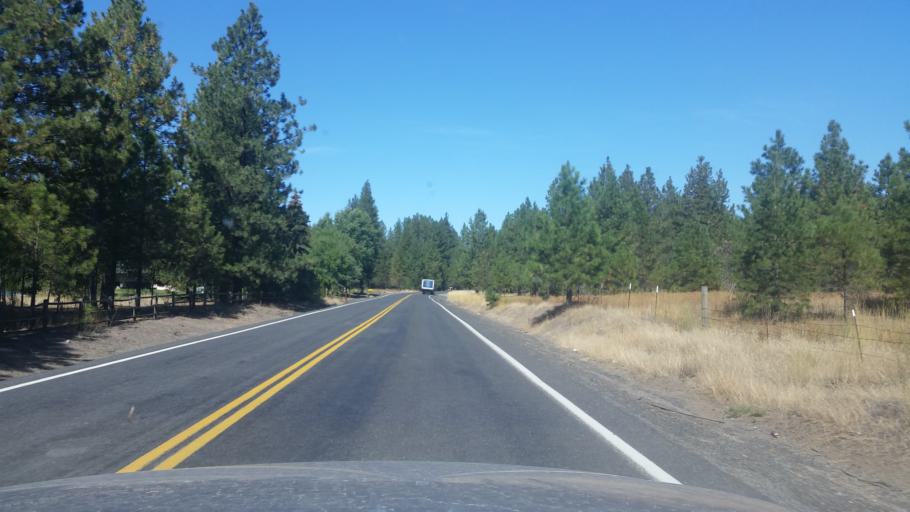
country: US
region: Washington
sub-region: Spokane County
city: Spokane
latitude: 47.5842
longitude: -117.4560
